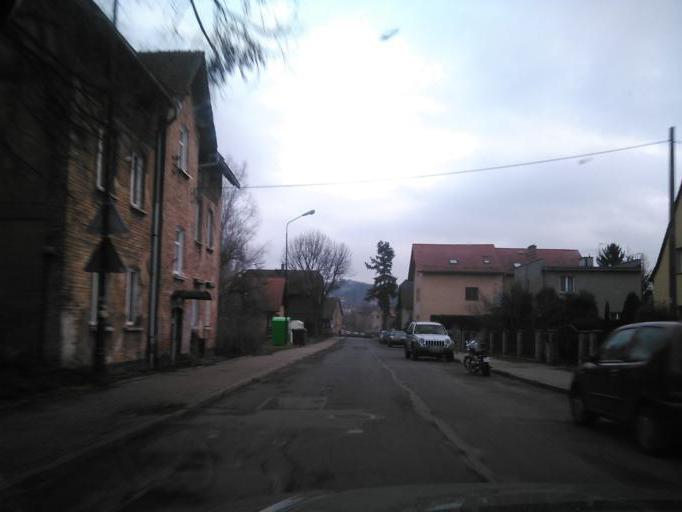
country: PL
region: Lower Silesian Voivodeship
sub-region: Jelenia Gora
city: Jelenia Gora
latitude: 50.9099
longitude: 15.7464
